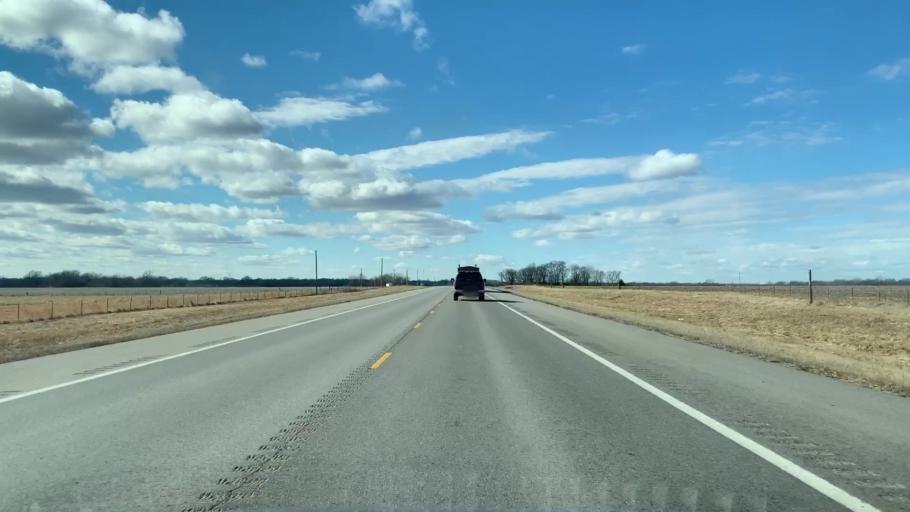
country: US
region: Kansas
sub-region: Cherokee County
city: Columbus
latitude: 37.3397
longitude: -94.8637
